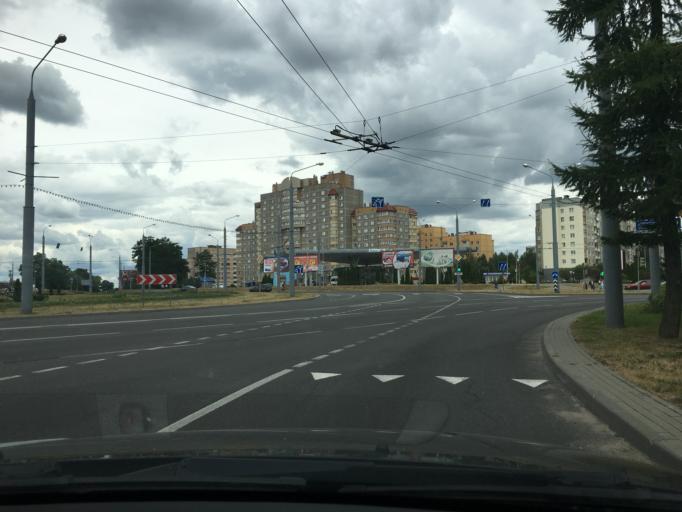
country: BY
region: Grodnenskaya
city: Hrodna
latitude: 53.6475
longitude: 23.8364
